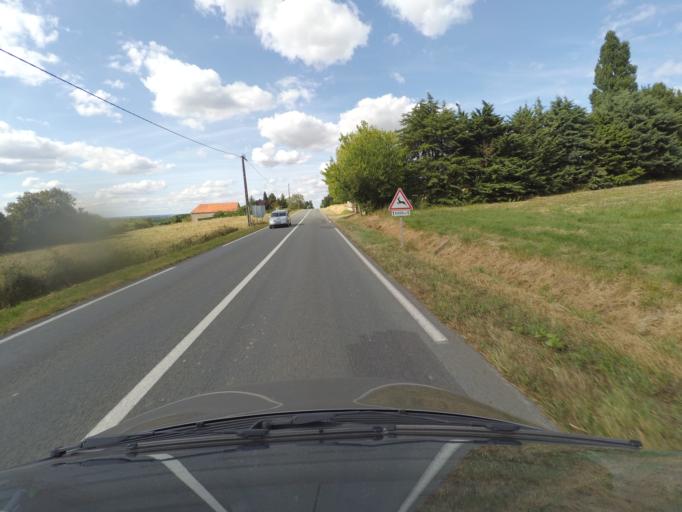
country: FR
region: Poitou-Charentes
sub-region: Departement de la Vienne
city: Vouneuil-sur-Vienne
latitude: 46.7275
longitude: 0.5534
